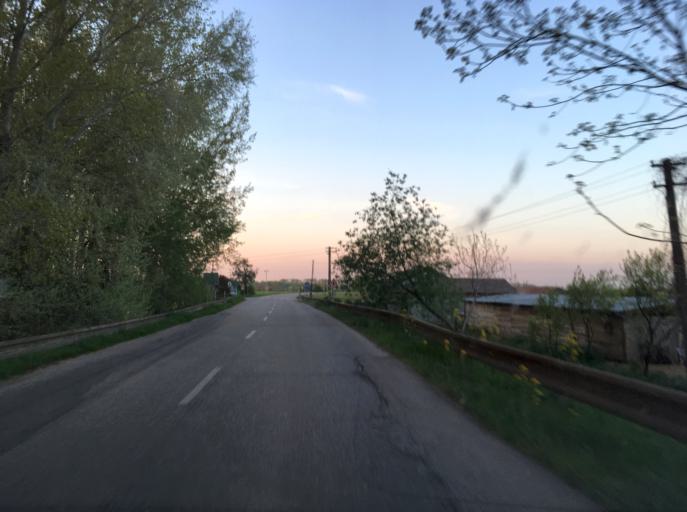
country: SK
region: Nitriansky
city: Kolarovo
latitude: 47.9241
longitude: 18.0161
